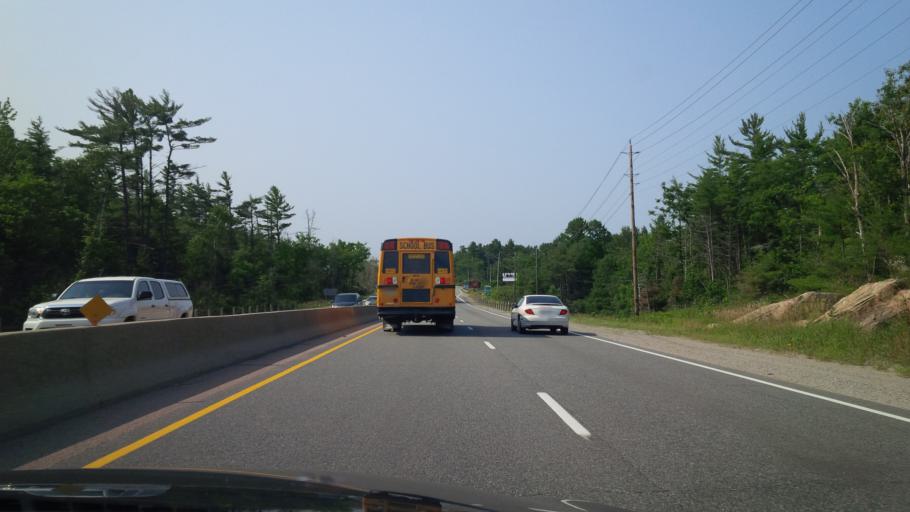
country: CA
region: Ontario
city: Gravenhurst
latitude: 44.7842
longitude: -79.3338
